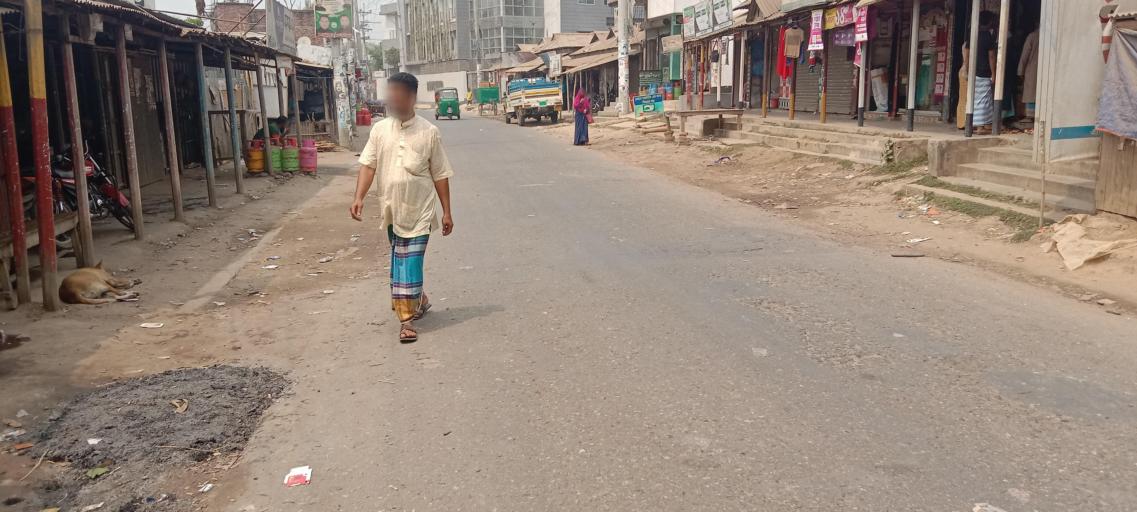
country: BD
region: Dhaka
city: Sakhipur
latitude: 24.4448
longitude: 90.3395
